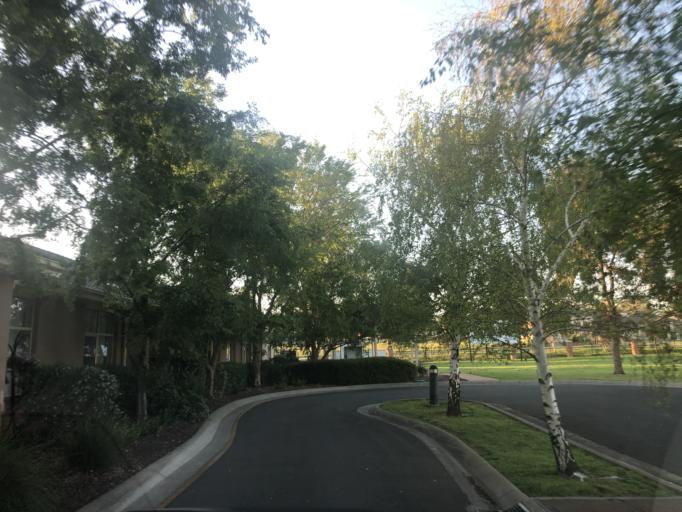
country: AU
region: Victoria
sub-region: Casey
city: Lynbrook
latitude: -38.0477
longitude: 145.2612
